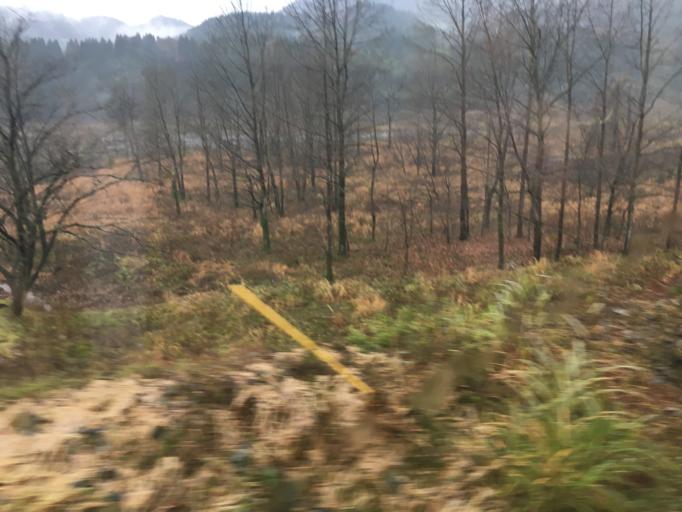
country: JP
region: Toyama
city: Kamiichi
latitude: 36.5754
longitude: 137.3968
